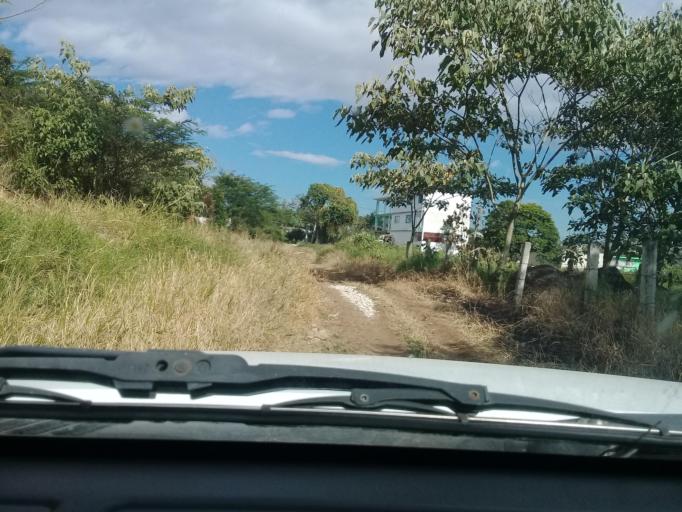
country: MX
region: Veracruz
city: El Castillo
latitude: 19.5428
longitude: -96.8781
